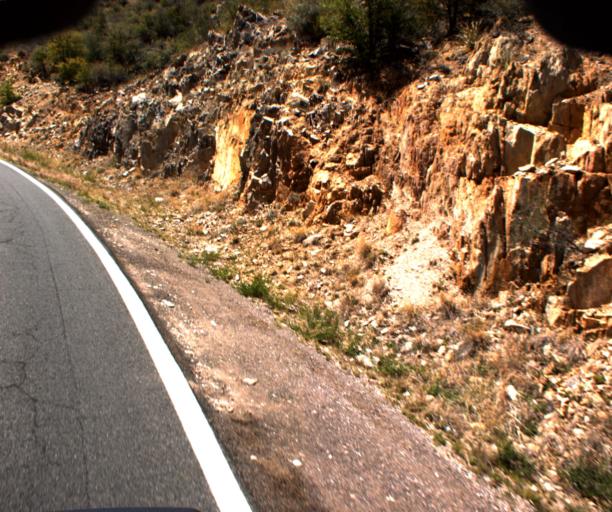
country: US
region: Arizona
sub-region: Yavapai County
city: Clarkdale
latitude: 34.7391
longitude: -112.1274
